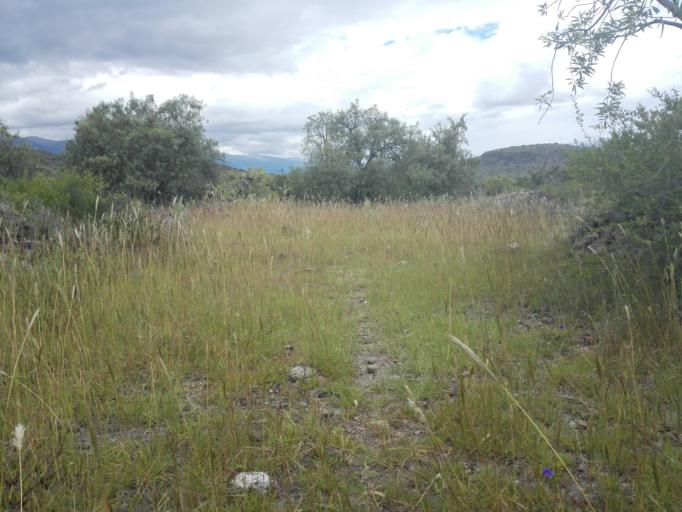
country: PE
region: Ayacucho
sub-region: Provincia de Huamanga
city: Pacaycasa
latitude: -13.0672
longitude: -74.1922
